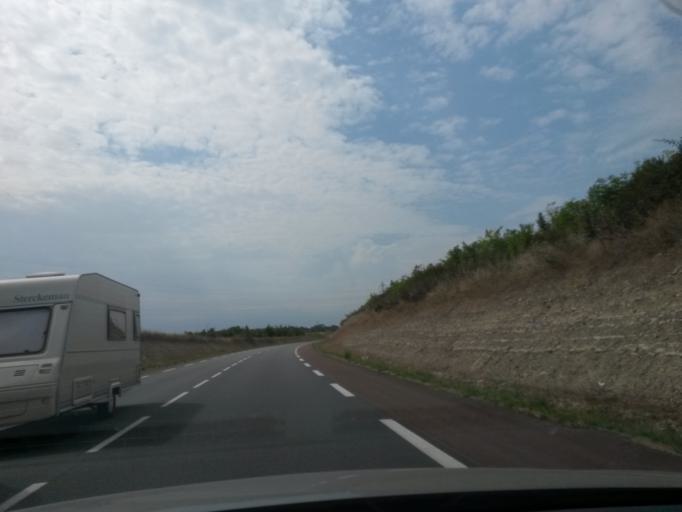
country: FR
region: Poitou-Charentes
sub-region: Departement de la Charente-Maritime
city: Saint-Xandre
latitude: 46.2039
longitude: -1.0903
